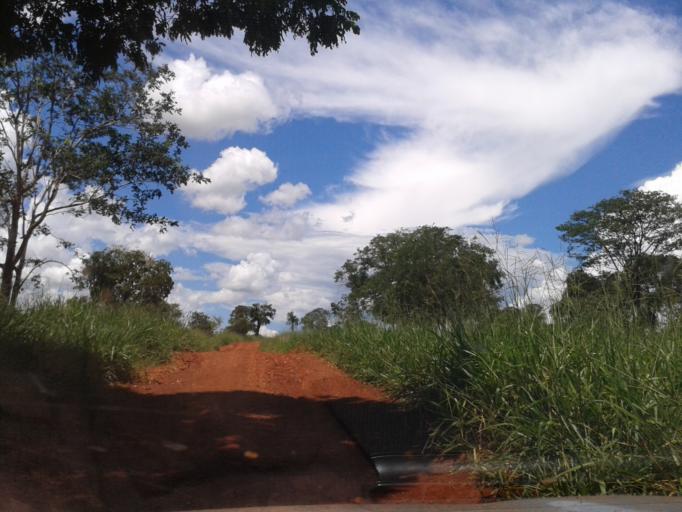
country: BR
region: Minas Gerais
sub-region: Capinopolis
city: Capinopolis
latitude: -18.7940
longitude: -49.8342
